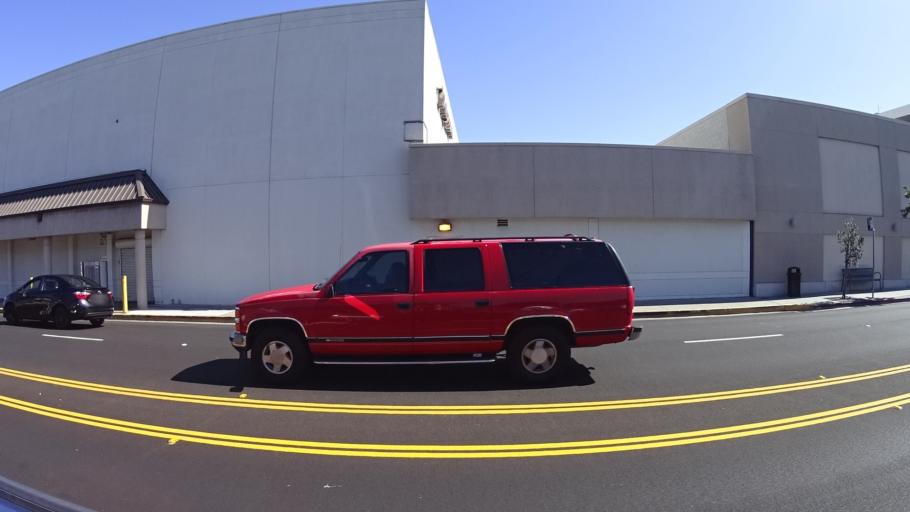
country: US
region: California
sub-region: San Mateo County
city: Broadmoor
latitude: 37.7005
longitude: -122.4845
